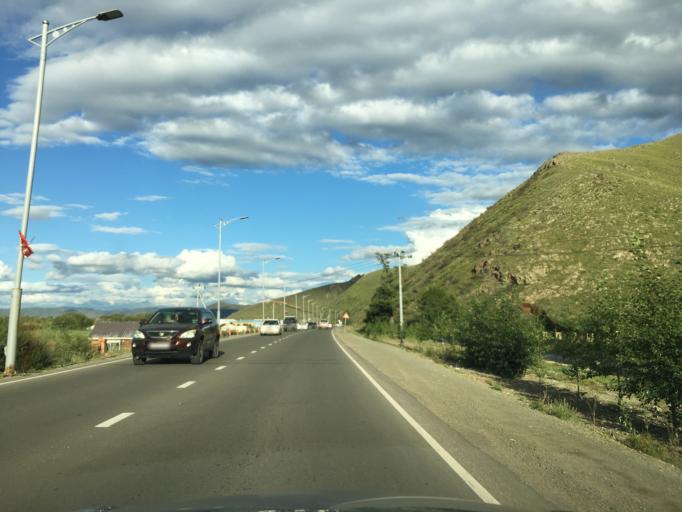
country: MN
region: Ulaanbaatar
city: Ulaanbaatar
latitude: 47.8827
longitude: 106.9641
